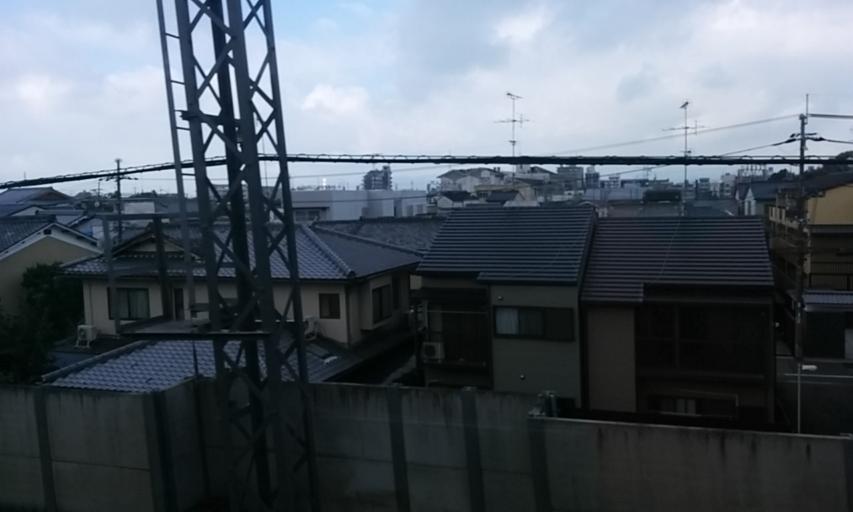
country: JP
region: Kyoto
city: Uji
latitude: 34.9290
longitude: 135.7653
